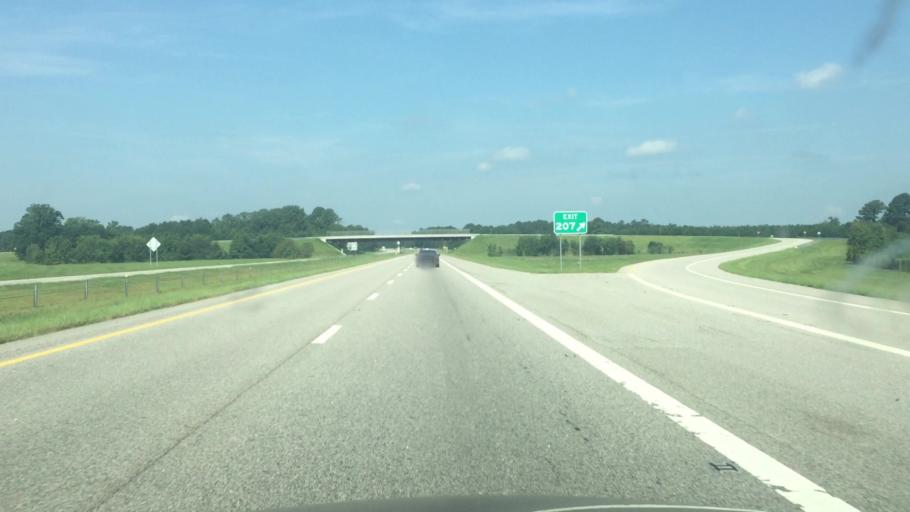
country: US
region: North Carolina
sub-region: Robeson County
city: Fairmont
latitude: 34.5969
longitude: -79.1294
